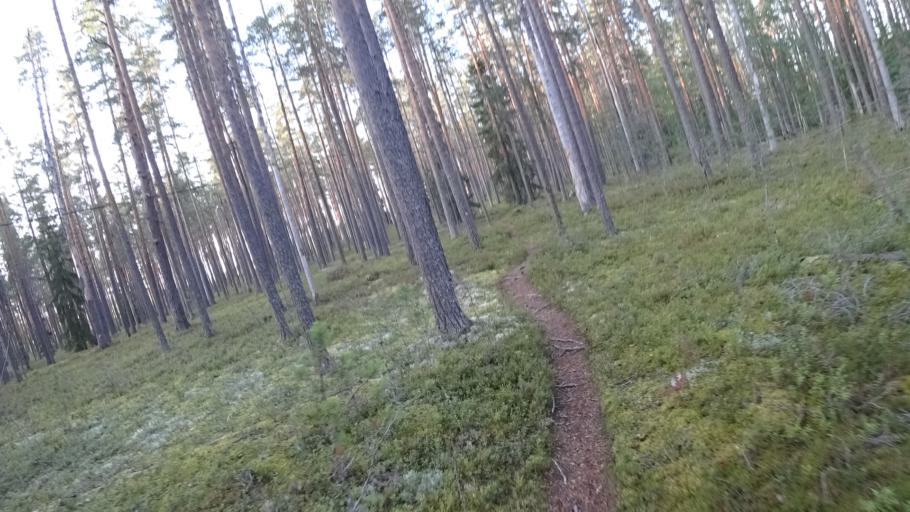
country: FI
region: North Karelia
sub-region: Joensuu
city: Ilomantsi
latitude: 62.5833
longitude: 31.1847
